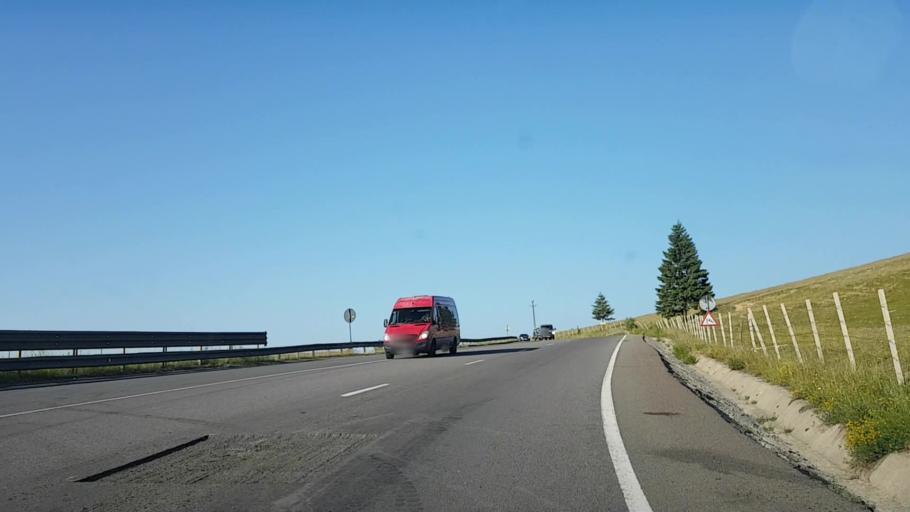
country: RO
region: Bistrita-Nasaud
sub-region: Comuna Lunca Ilvei
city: Lunca Ilvei
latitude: 47.2482
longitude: 25.0207
